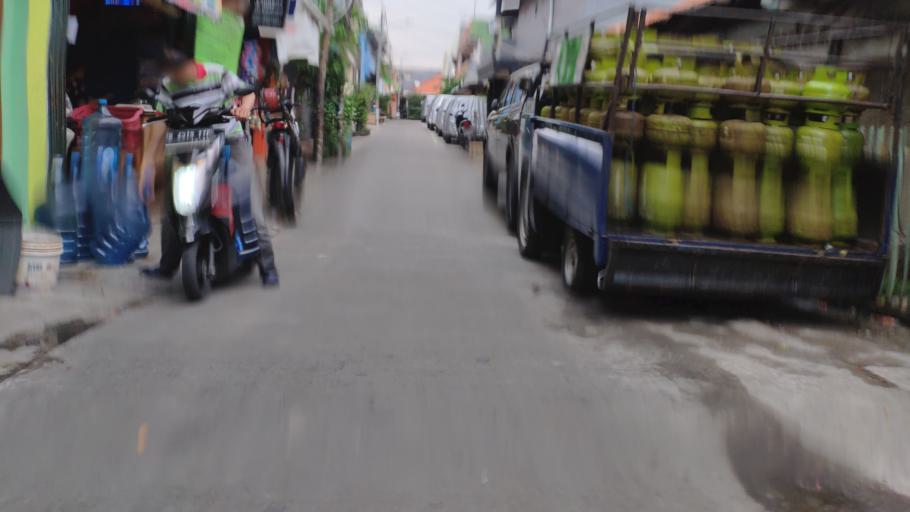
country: ID
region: Jakarta Raya
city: Jakarta
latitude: -6.2006
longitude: 106.8580
